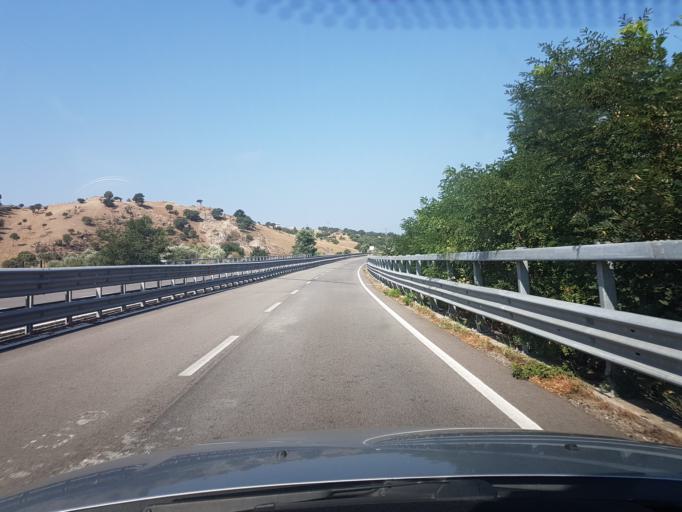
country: IT
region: Sardinia
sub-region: Provincia di Nuoro
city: Nuoro
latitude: 40.3131
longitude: 9.2401
